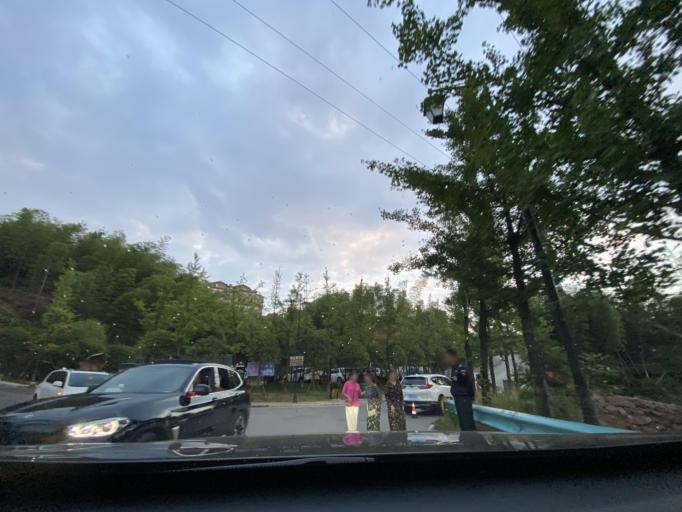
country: CN
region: Guizhou Sheng
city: Changqi
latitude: 28.5395
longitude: 105.9869
